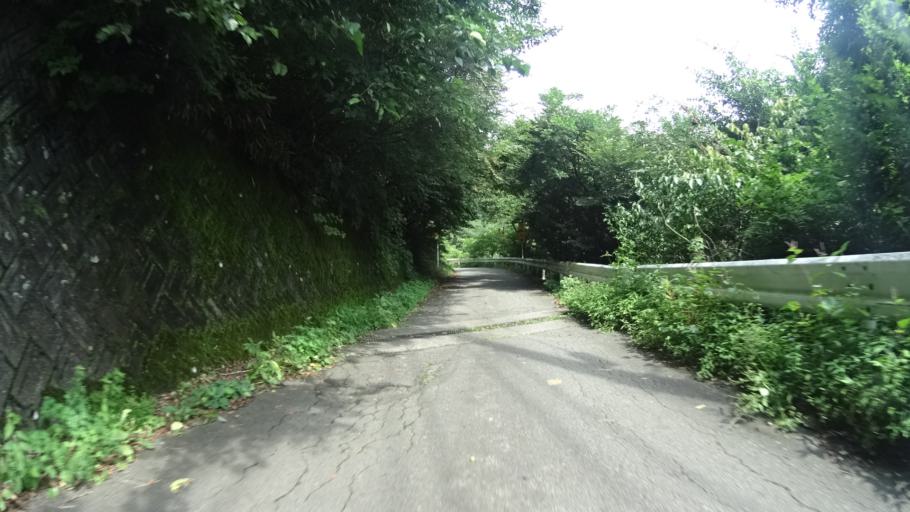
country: JP
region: Yamanashi
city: Nirasaki
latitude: 35.9026
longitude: 138.4207
